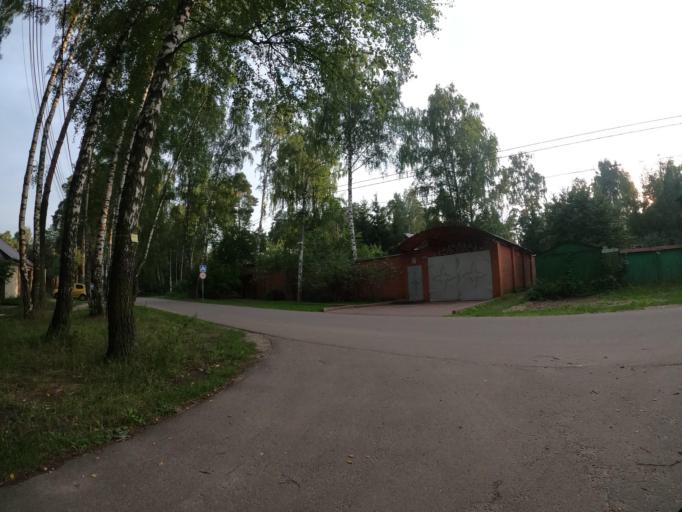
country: RU
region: Moskovskaya
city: Bykovo
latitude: 55.6375
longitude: 38.0833
